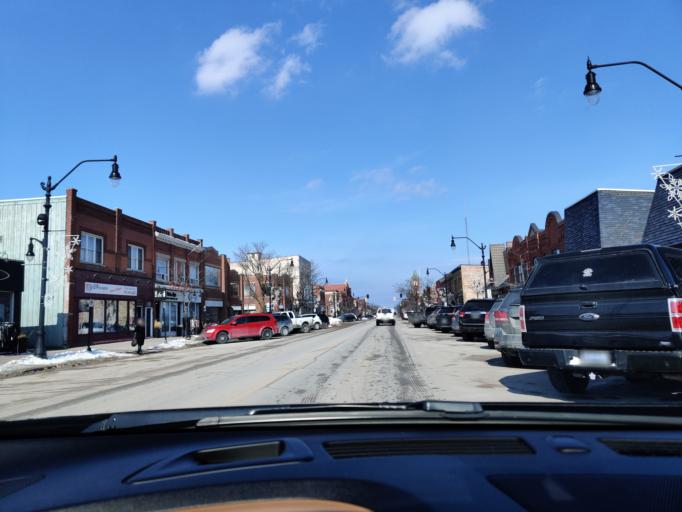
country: CA
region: Ontario
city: Collingwood
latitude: 44.4975
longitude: -80.2164
